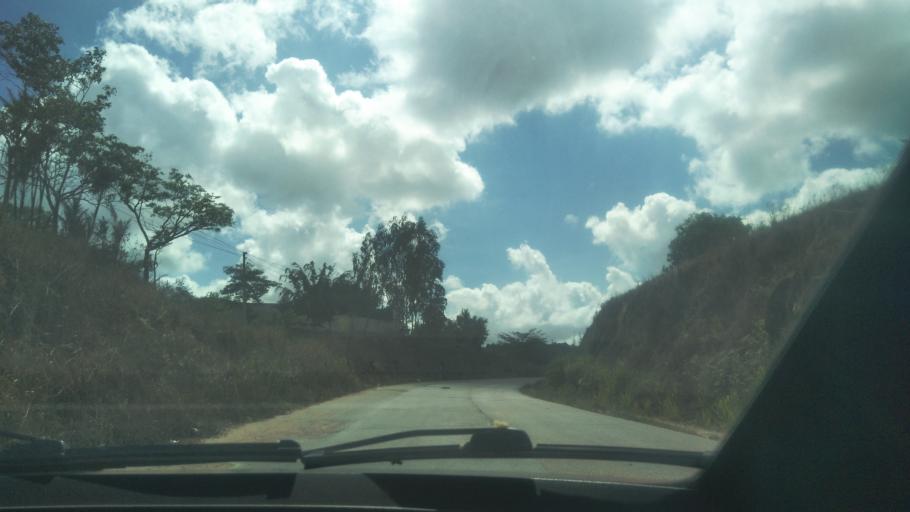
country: BR
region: Pernambuco
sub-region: Vitoria De Santo Antao
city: Vitoria de Santo Antao
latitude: -8.1385
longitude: -35.2745
